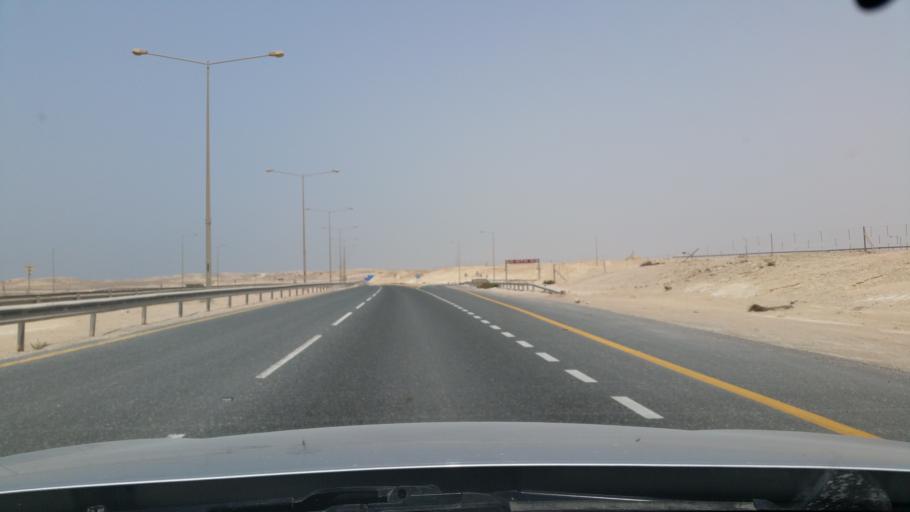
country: QA
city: Umm Bab
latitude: 25.2597
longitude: 50.7960
